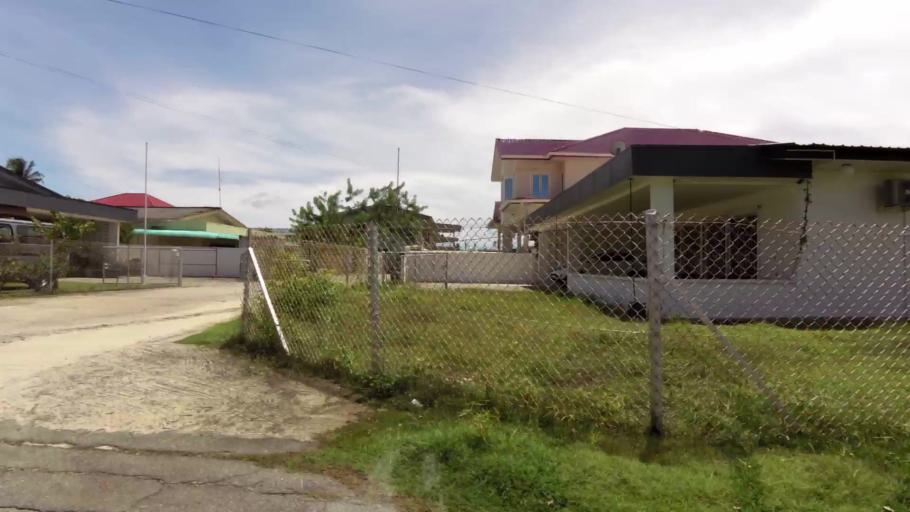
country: BN
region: Belait
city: Kuala Belait
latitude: 4.5932
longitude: 114.2393
